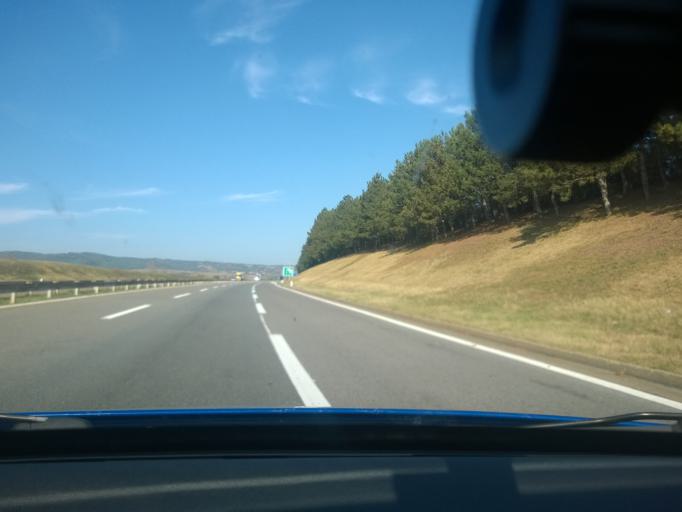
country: RS
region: Central Serbia
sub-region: Nisavski Okrug
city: Razanj
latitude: 43.6369
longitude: 21.5599
